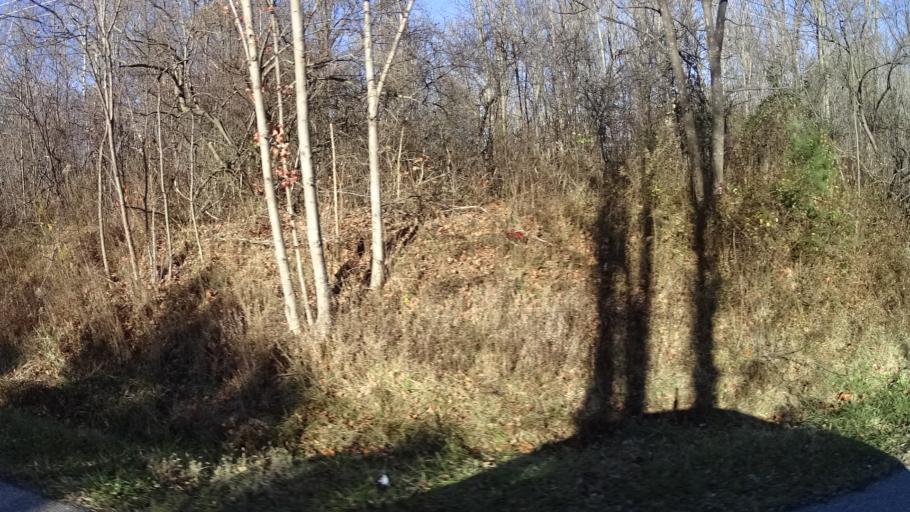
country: US
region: Ohio
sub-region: Lorain County
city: Elyria
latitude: 41.3121
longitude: -82.1351
